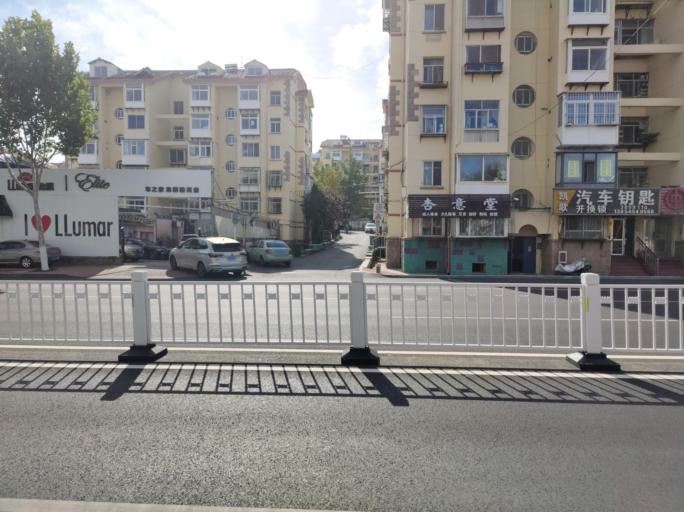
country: CN
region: Shandong Sheng
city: Xiangyang
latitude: 37.5197
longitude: 121.3898
